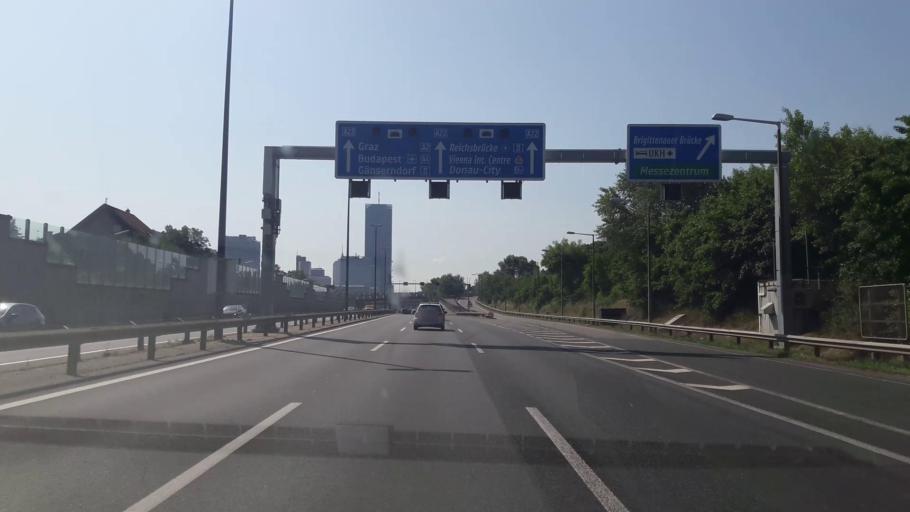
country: AT
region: Vienna
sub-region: Wien Stadt
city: Vienna
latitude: 48.2436
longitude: 16.3981
